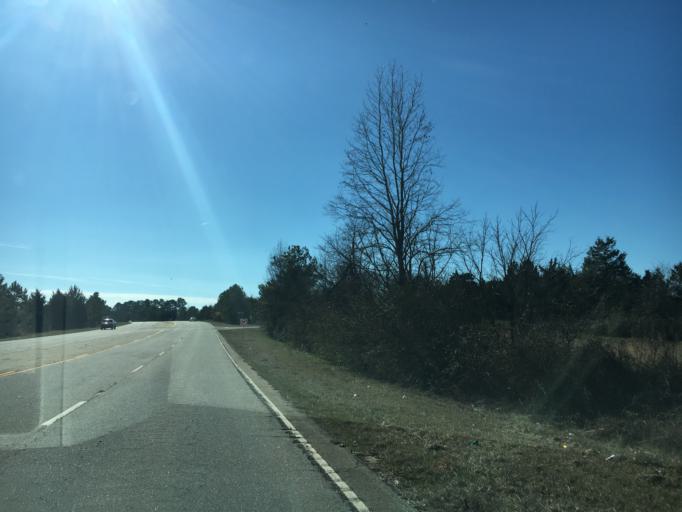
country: US
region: South Carolina
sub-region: Anderson County
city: Homeland Park
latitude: 34.3956
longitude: -82.6908
